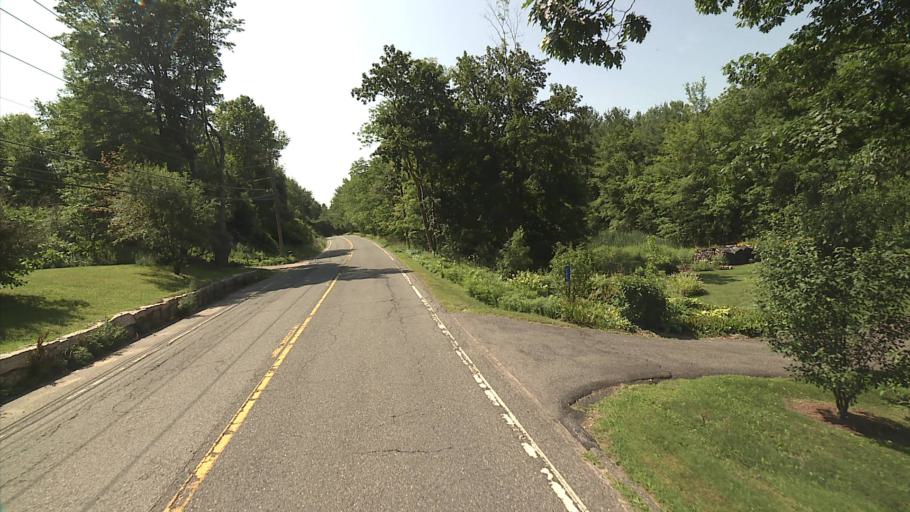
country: US
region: Connecticut
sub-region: Litchfield County
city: Winchester Center
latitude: 41.9696
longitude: -73.1996
